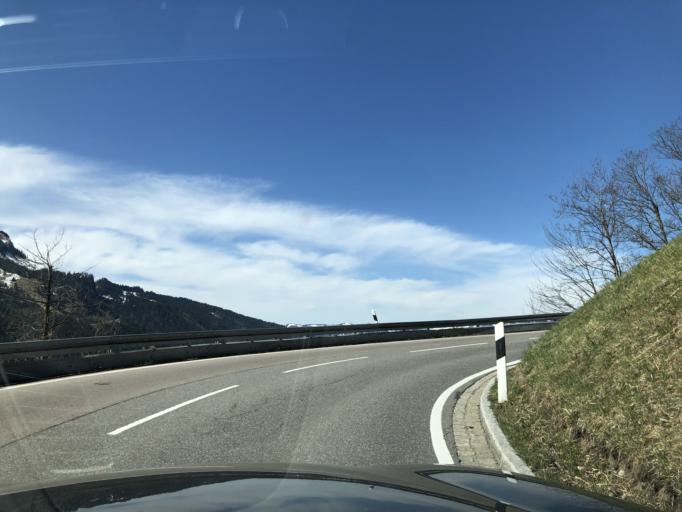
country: AT
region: Tyrol
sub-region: Politischer Bezirk Reutte
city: Schattwald
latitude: 47.5064
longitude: 10.3879
